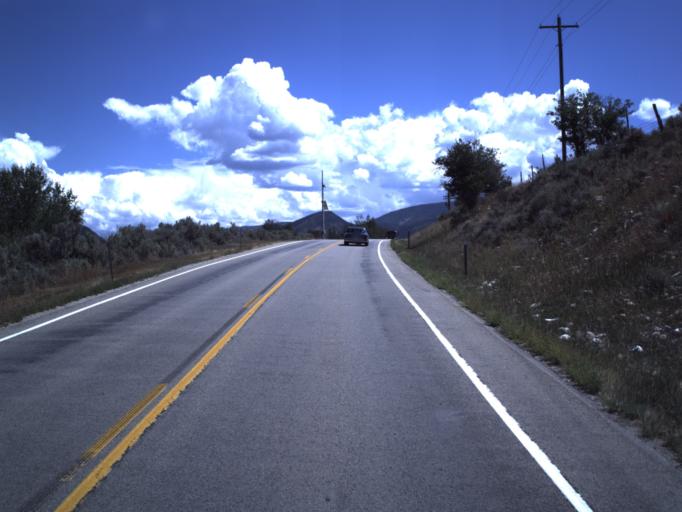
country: US
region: Utah
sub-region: Summit County
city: Oakley
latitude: 40.7238
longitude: -111.3178
